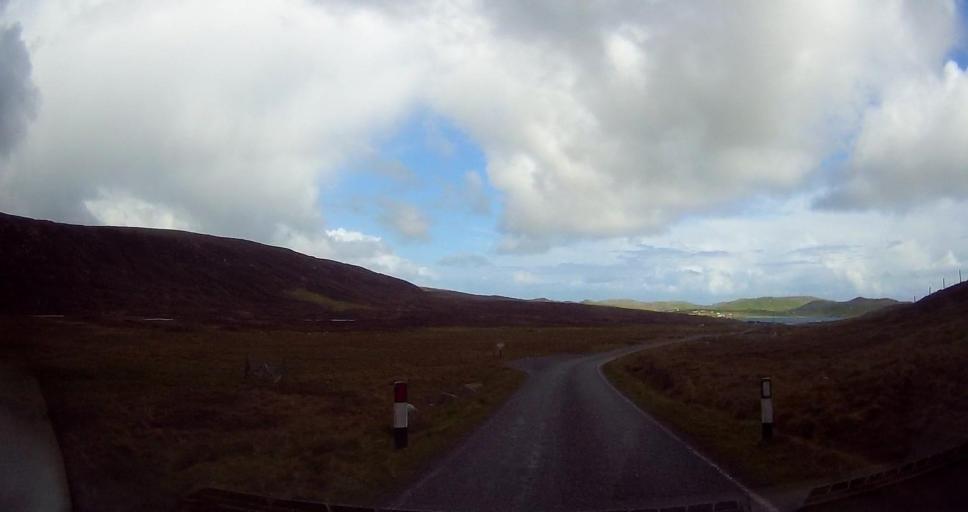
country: GB
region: Scotland
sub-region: Shetland Islands
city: Lerwick
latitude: 60.5641
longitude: -1.3348
